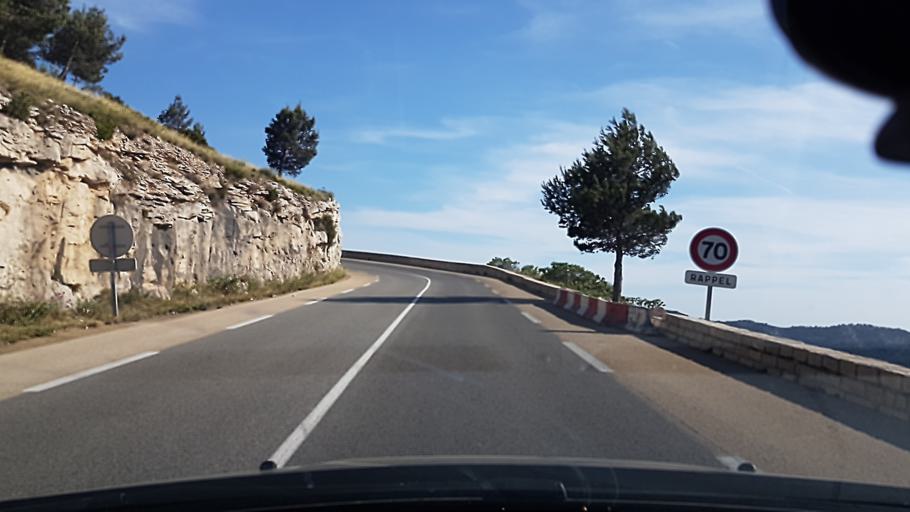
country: FR
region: Provence-Alpes-Cote d'Azur
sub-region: Departement des Bouches-du-Rhone
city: Marseille 09
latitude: 43.2439
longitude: 5.4453
